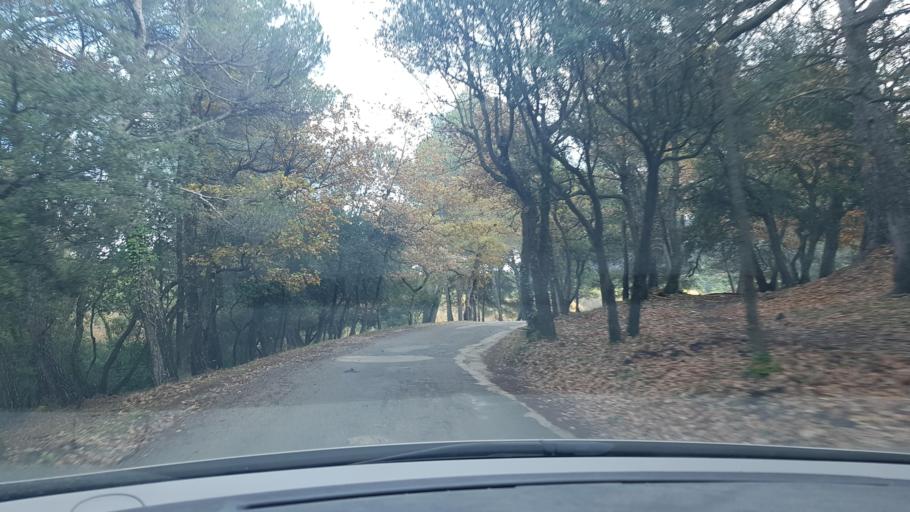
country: FR
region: Provence-Alpes-Cote d'Azur
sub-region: Departement des Bouches-du-Rhone
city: Simiane-Collongue
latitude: 43.4147
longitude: 5.4671
